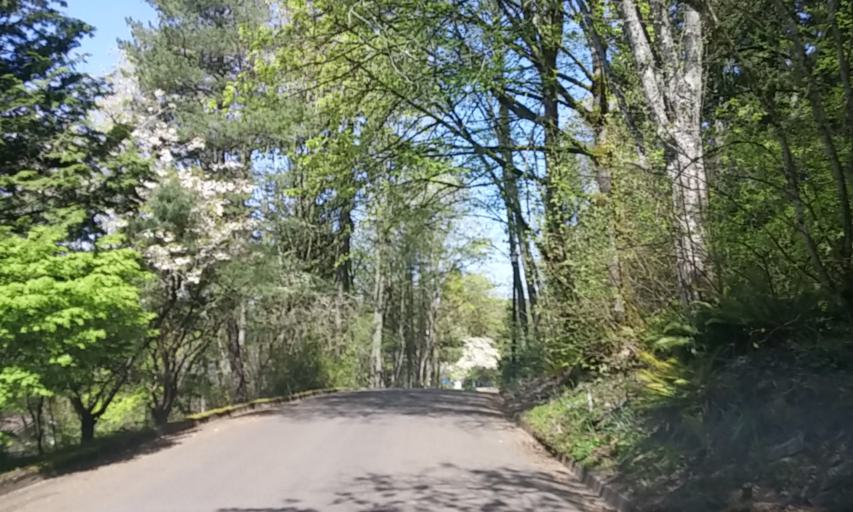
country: US
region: Oregon
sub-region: Washington County
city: West Haven-Sylvan
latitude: 45.5171
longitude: -122.7643
